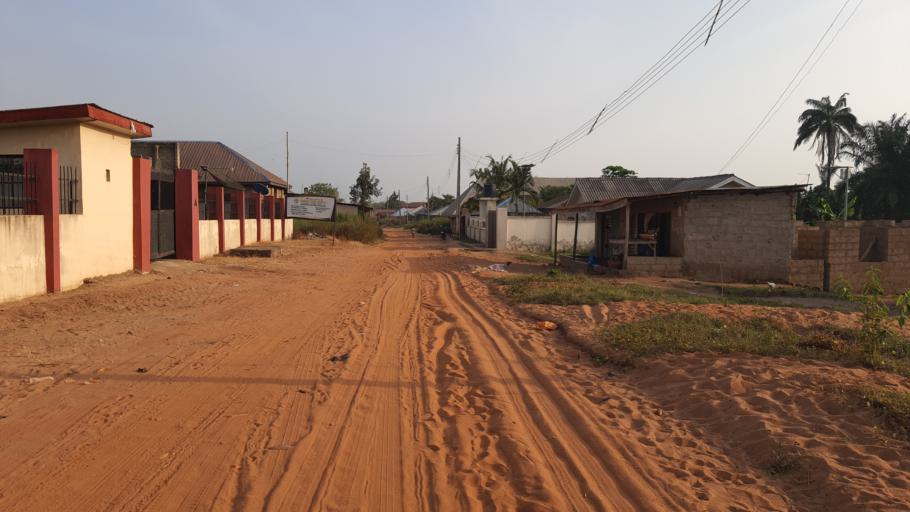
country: NG
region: Osun
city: Iwo
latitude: 7.6241
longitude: 4.1584
